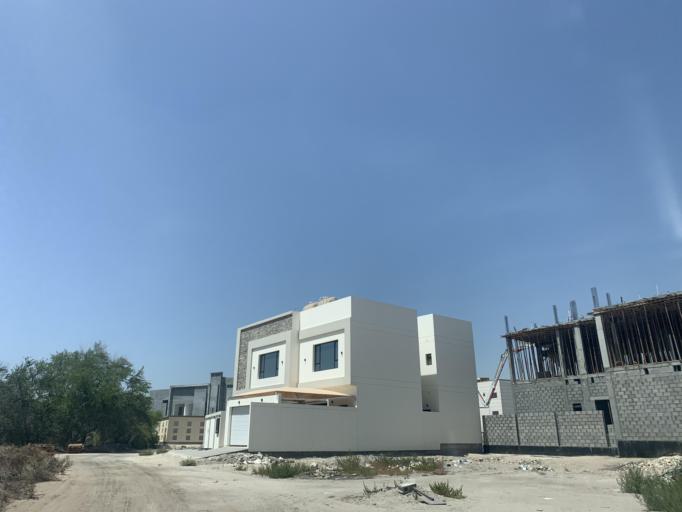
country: BH
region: Manama
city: Jidd Hafs
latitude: 26.2223
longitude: 50.5091
